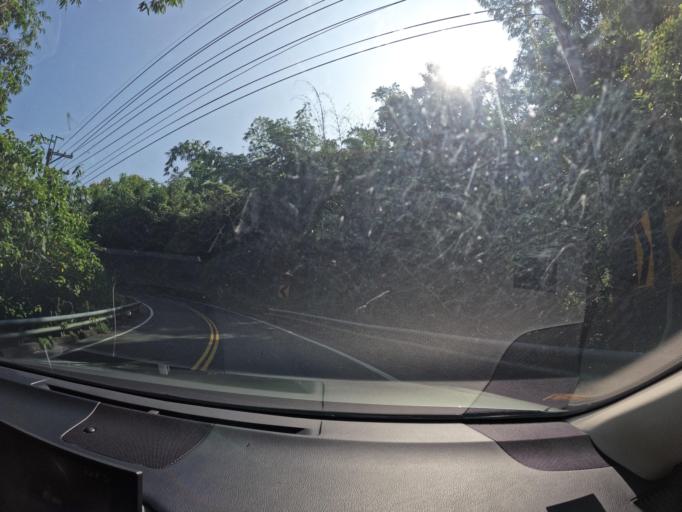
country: TW
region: Taiwan
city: Yujing
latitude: 23.0737
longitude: 120.6088
